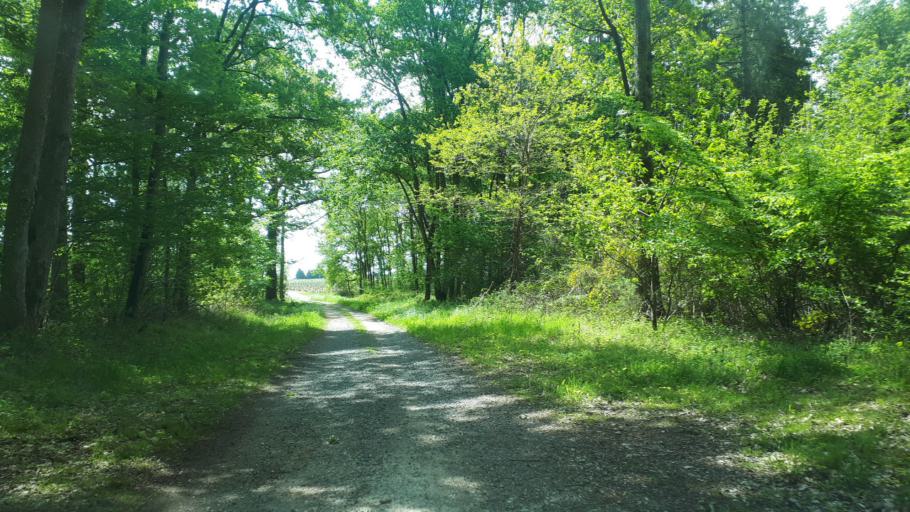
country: FR
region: Centre
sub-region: Departement du Loir-et-Cher
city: Saint-Romain-sur-Cher
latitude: 47.3600
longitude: 1.4295
